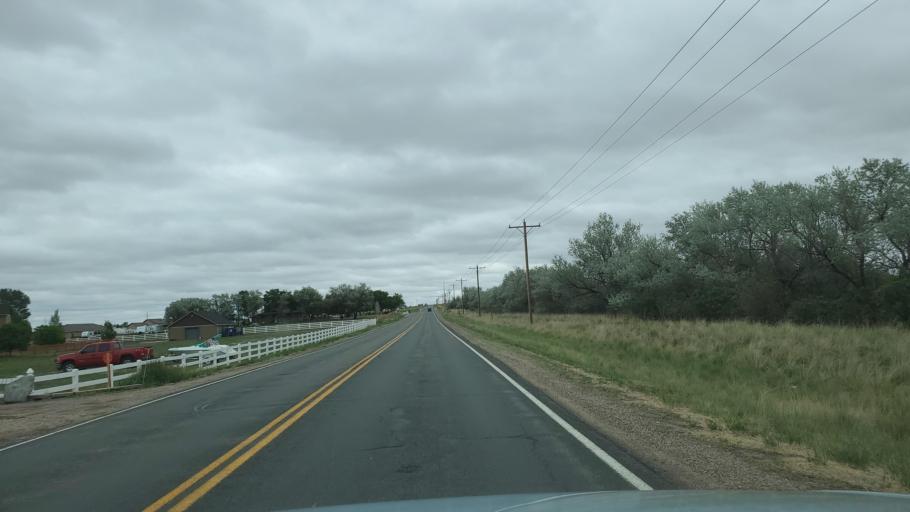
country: US
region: Colorado
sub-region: Weld County
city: Lochbuie
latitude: 39.9725
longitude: -104.7022
